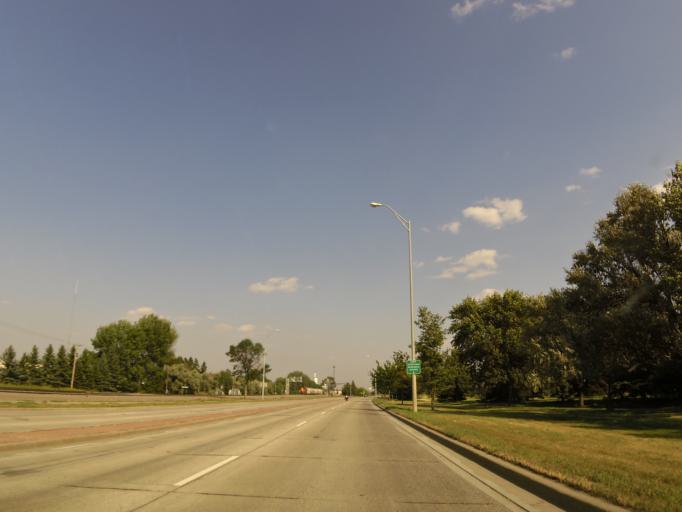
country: US
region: North Dakota
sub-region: Grand Forks County
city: Grand Forks
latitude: 47.9182
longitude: -97.0859
